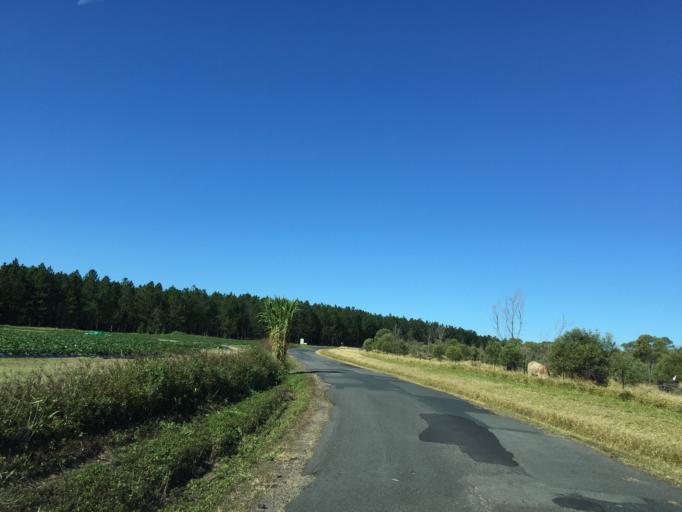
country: AU
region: Queensland
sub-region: Moreton Bay
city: Caboolture
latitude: -27.0234
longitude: 152.9857
